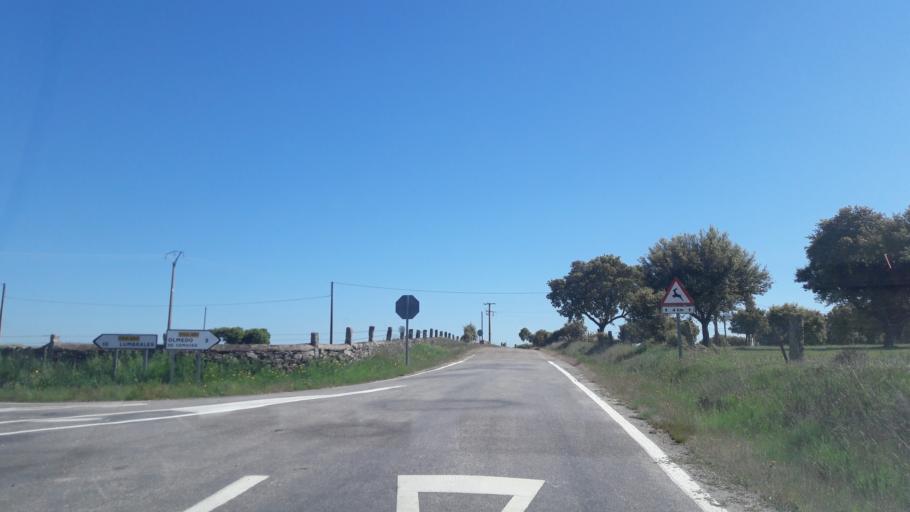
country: ES
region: Castille and Leon
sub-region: Provincia de Salamanca
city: Olmedo de Camaces
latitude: 40.8706
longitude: -6.6422
